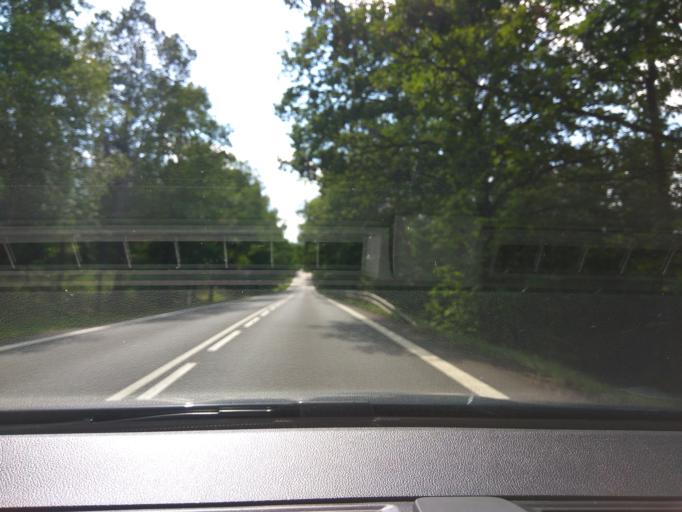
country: CZ
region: Jihocesky
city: Cimelice
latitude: 49.5010
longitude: 14.1438
